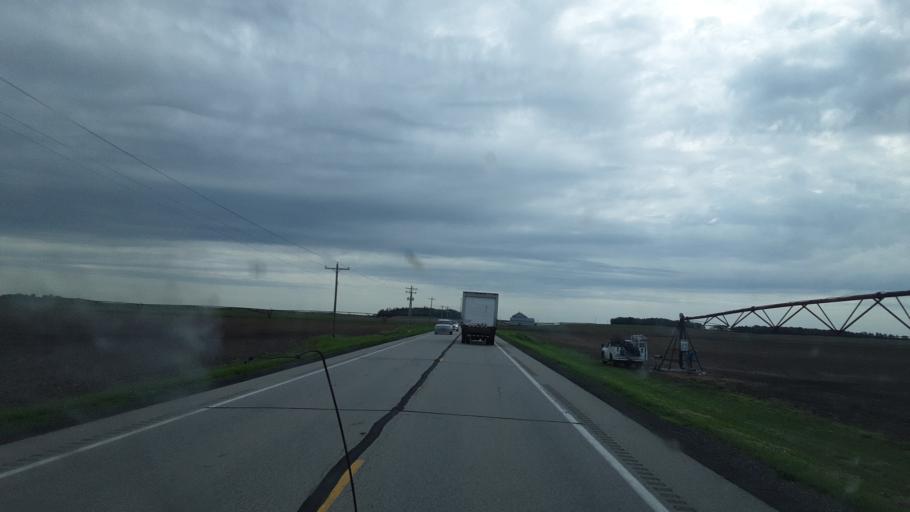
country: US
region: Illinois
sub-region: Mason County
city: Manito
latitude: 40.3032
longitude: -89.8005
